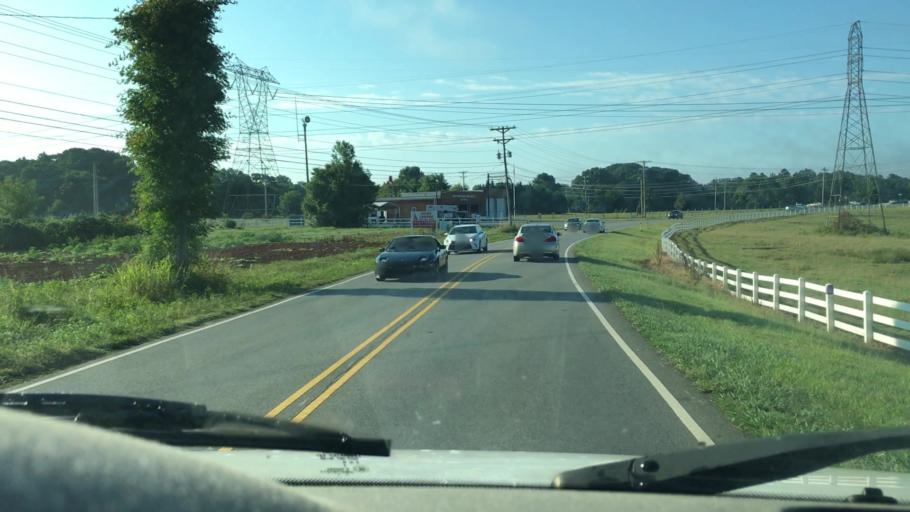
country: US
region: North Carolina
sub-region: Mecklenburg County
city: Huntersville
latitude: 35.4249
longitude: -80.9165
